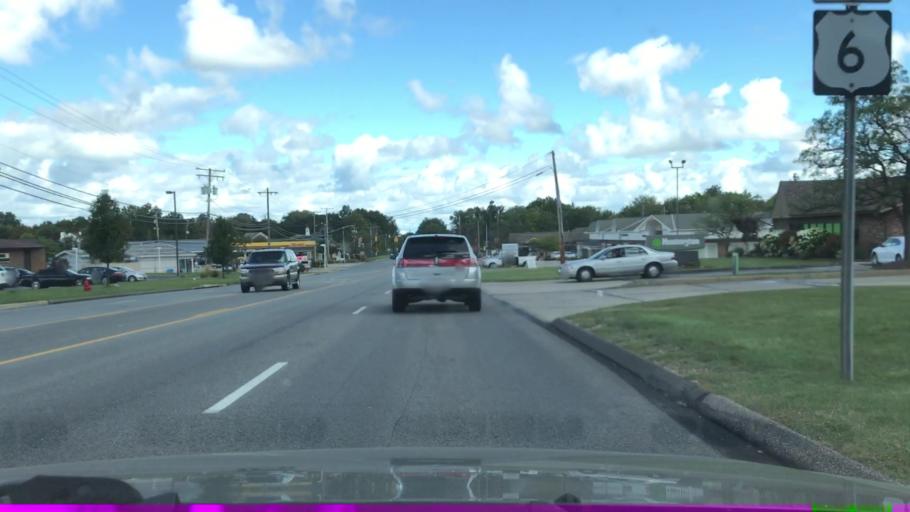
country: US
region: Ohio
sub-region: Lake County
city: Wickliffe
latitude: 41.5858
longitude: -81.4394
